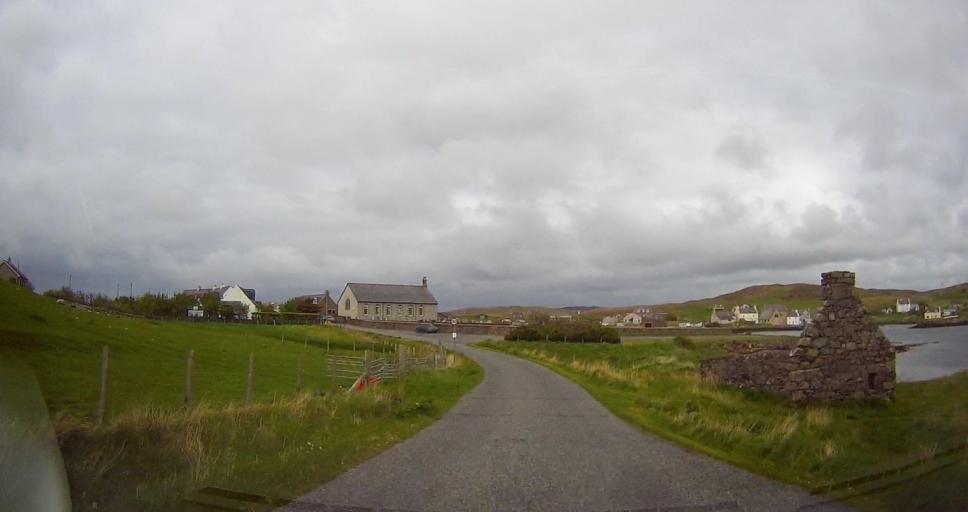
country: GB
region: Scotland
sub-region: Shetland Islands
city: Sandwick
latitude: 60.2263
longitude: -1.5692
